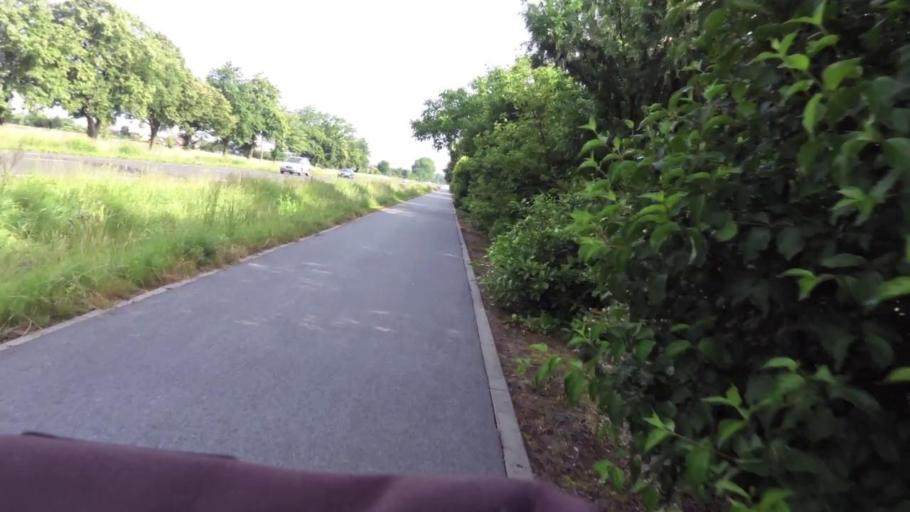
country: PL
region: West Pomeranian Voivodeship
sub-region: Powiat kamienski
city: Dziwnow
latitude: 54.0186
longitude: 14.8110
